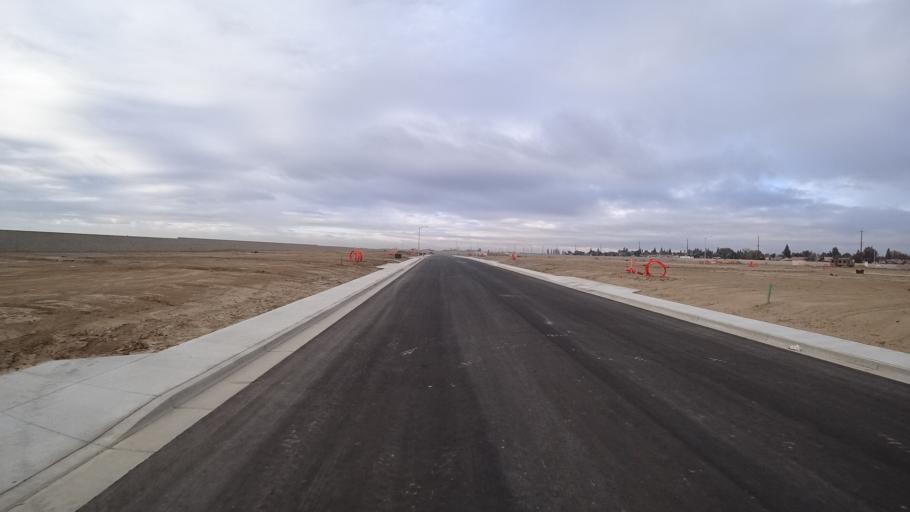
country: US
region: California
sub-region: Kern County
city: Greenfield
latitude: 35.2939
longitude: -119.0803
